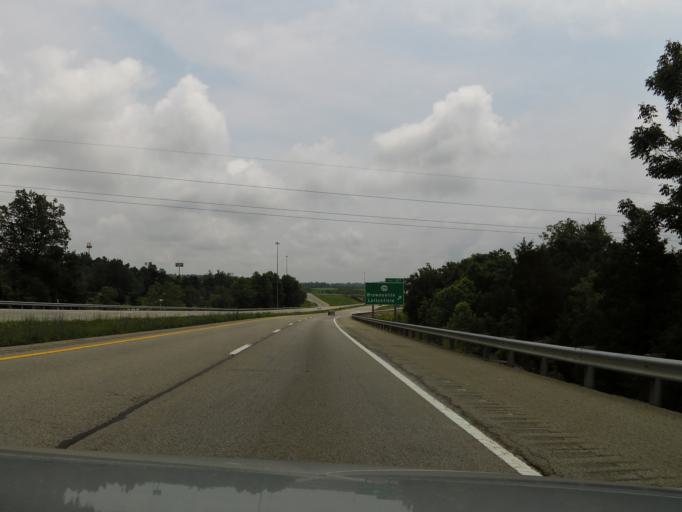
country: US
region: Kentucky
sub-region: Grayson County
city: Leitchfield
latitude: 37.4652
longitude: -86.2987
